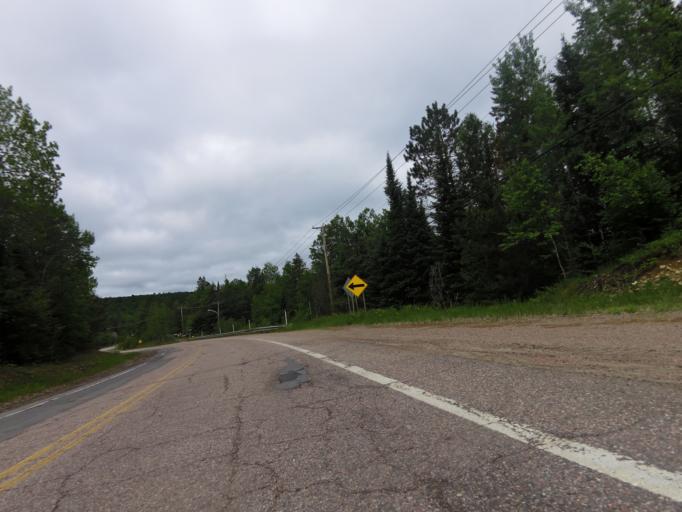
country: CA
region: Quebec
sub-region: Outaouais
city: Shawville
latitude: 45.8391
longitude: -76.4521
